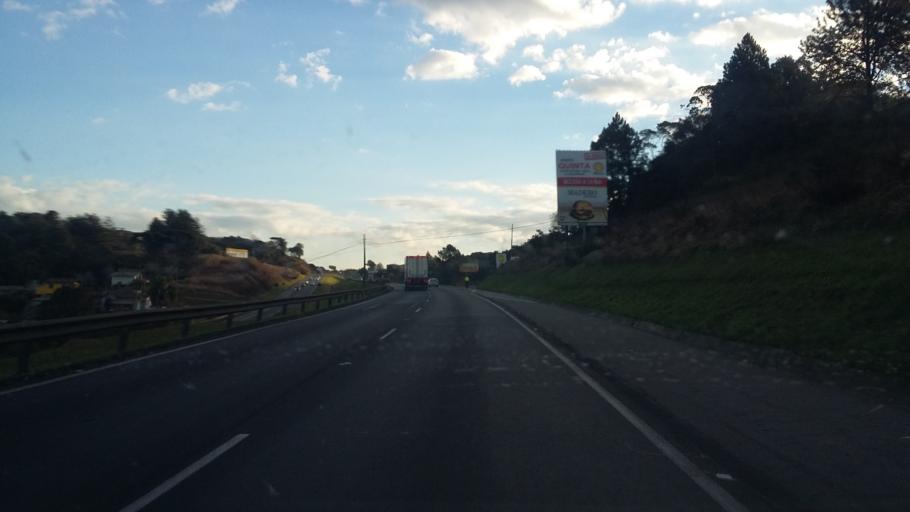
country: BR
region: Parana
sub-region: Curitiba
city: Curitiba
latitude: -25.4285
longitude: -49.3926
